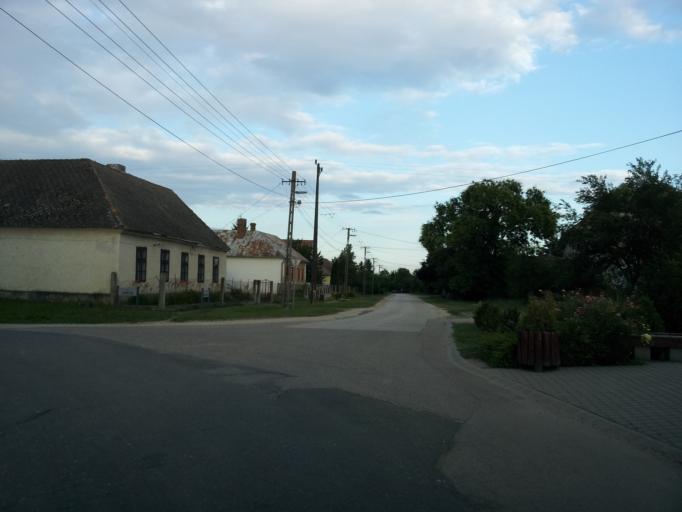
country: HU
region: Somogy
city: Balatonszabadi
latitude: 46.8832
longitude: 18.1537
